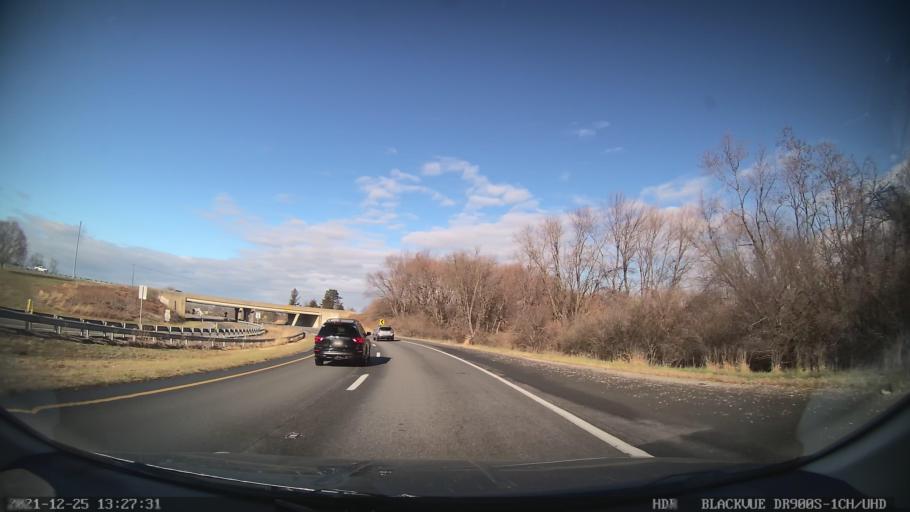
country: US
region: Pennsylvania
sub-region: York County
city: Shiloh
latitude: 39.9357
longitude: -76.7979
